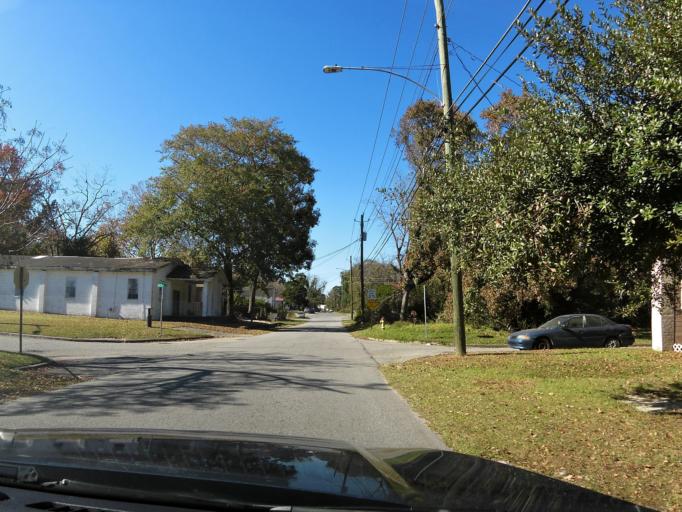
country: US
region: Georgia
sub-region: Chatham County
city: Savannah
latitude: 32.0740
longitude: -81.1165
